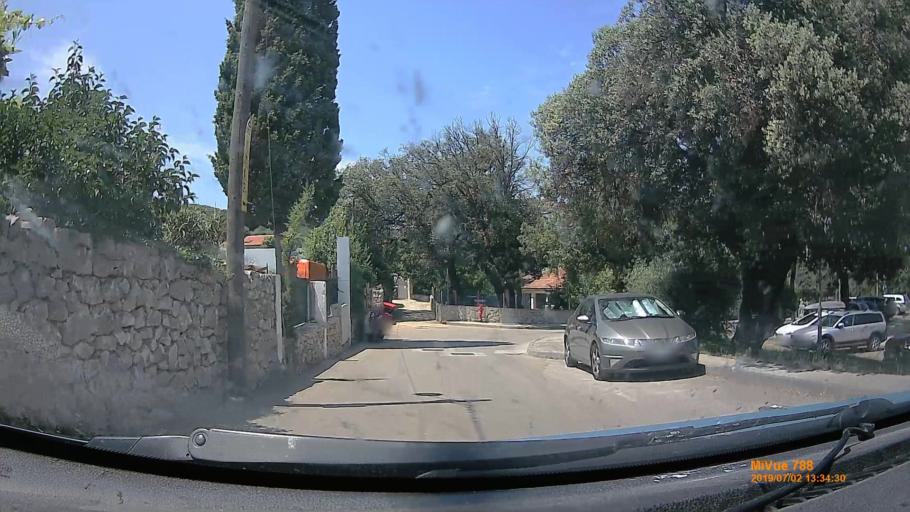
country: HR
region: Primorsko-Goranska
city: Mali Losinj
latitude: 44.5171
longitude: 14.5041
